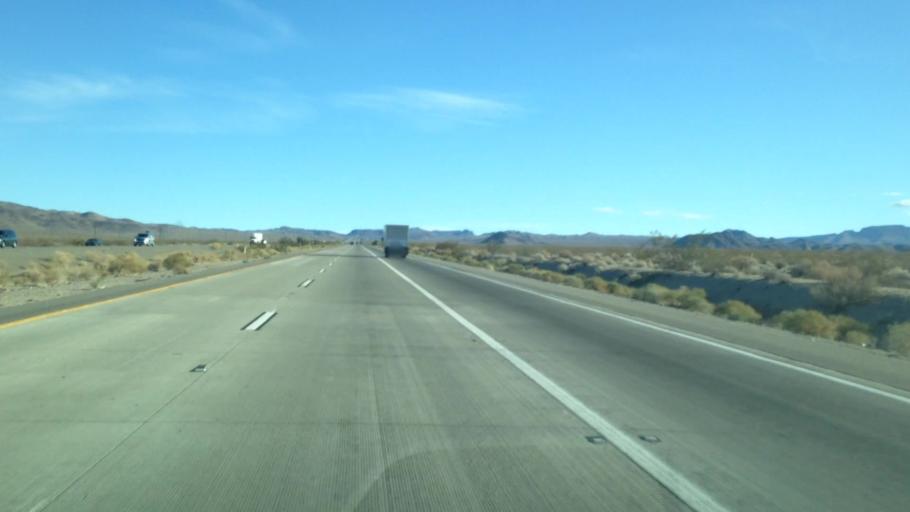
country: US
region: Nevada
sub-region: Clark County
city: Sandy Valley
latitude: 35.3238
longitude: -115.9824
